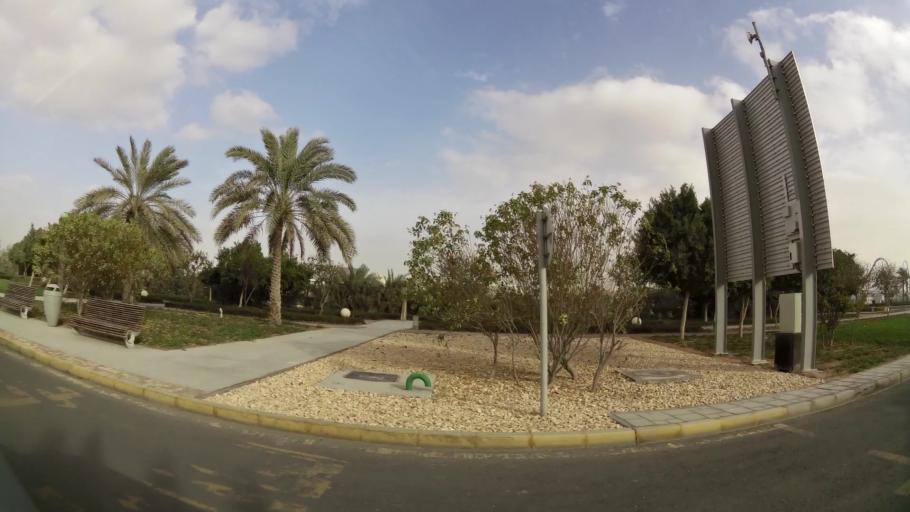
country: AE
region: Abu Dhabi
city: Abu Dhabi
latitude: 24.4901
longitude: 54.6024
